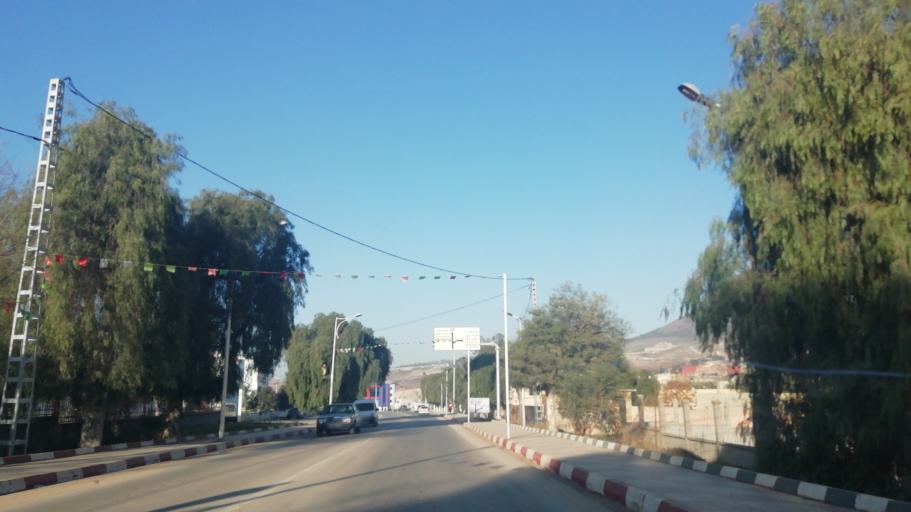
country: MA
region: Oriental
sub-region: Berkane-Taourirt
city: Ahfir
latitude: 34.9609
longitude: -2.0293
